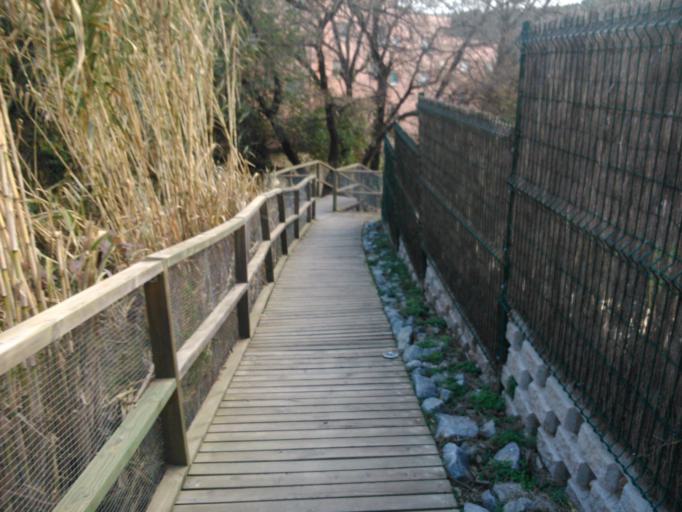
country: ES
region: Catalonia
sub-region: Provincia de Barcelona
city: Cervello
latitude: 41.4125
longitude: 1.9709
